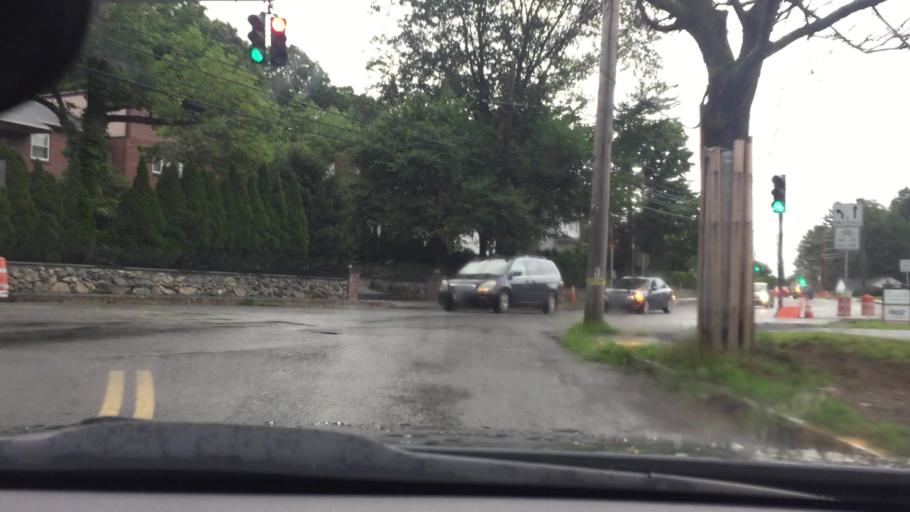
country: US
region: Massachusetts
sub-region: Middlesex County
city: Newton
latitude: 42.3000
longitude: -71.1881
